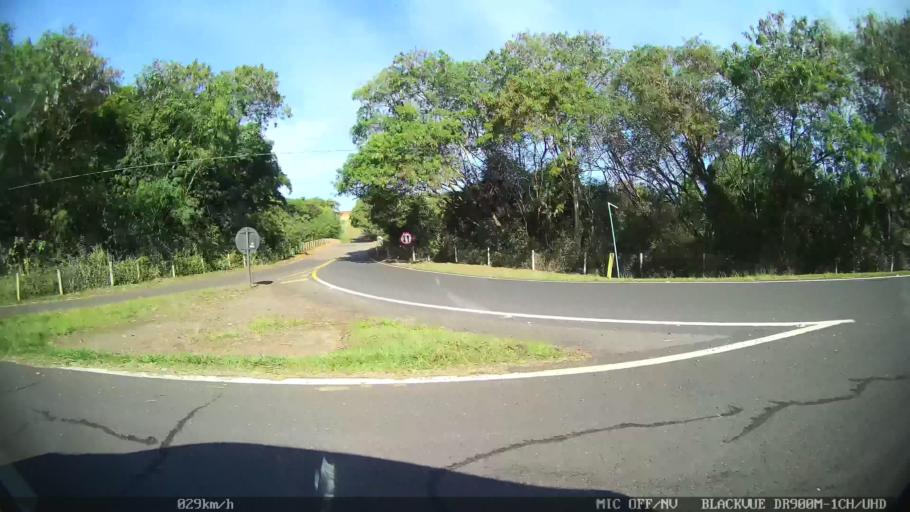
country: BR
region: Sao Paulo
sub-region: Piracicaba
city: Piracicaba
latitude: -22.6887
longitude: -47.5839
